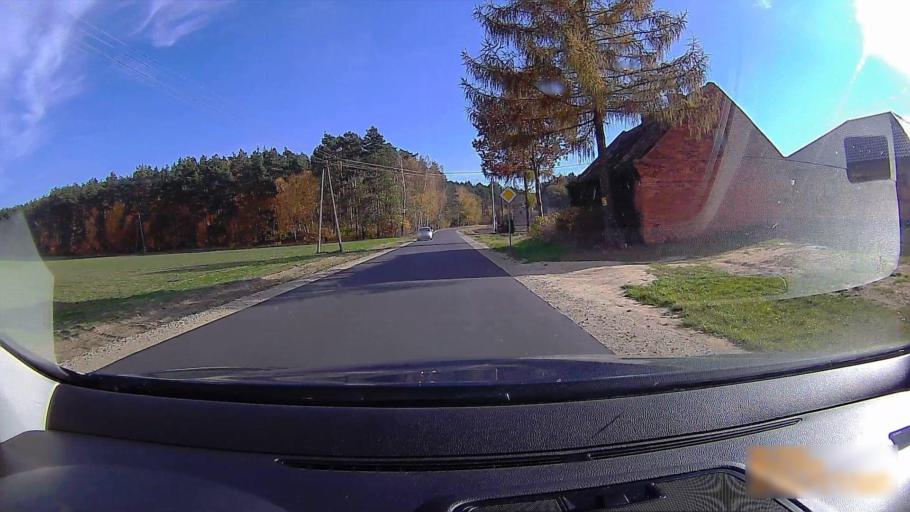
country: PL
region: Greater Poland Voivodeship
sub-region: Powiat ostrzeszowski
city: Ostrzeszow
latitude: 51.4112
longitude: 17.9904
